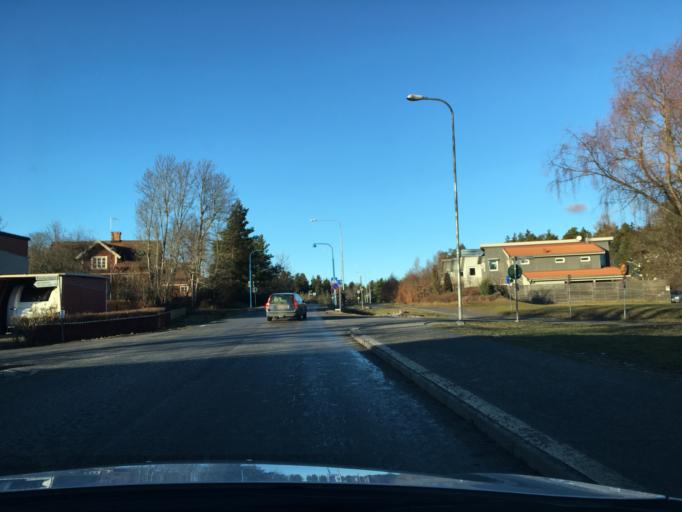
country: SE
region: Uppsala
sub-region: Knivsta Kommun
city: Knivsta
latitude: 59.7253
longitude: 17.7826
